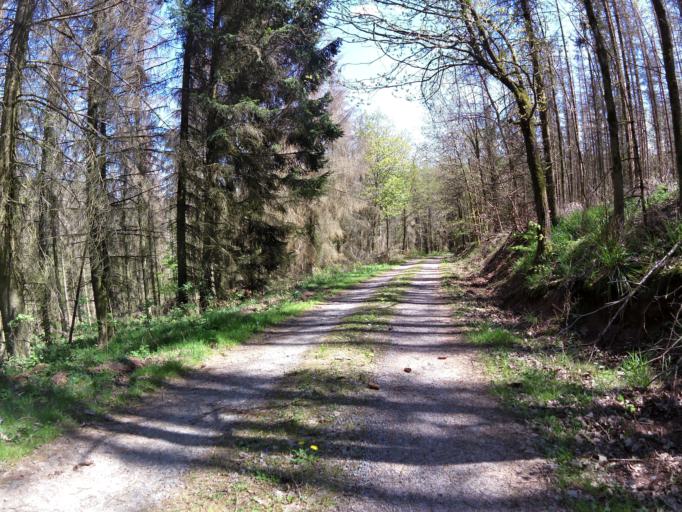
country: DE
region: Thuringia
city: Wolfsburg-Unkeroda
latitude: 50.9633
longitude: 10.2737
